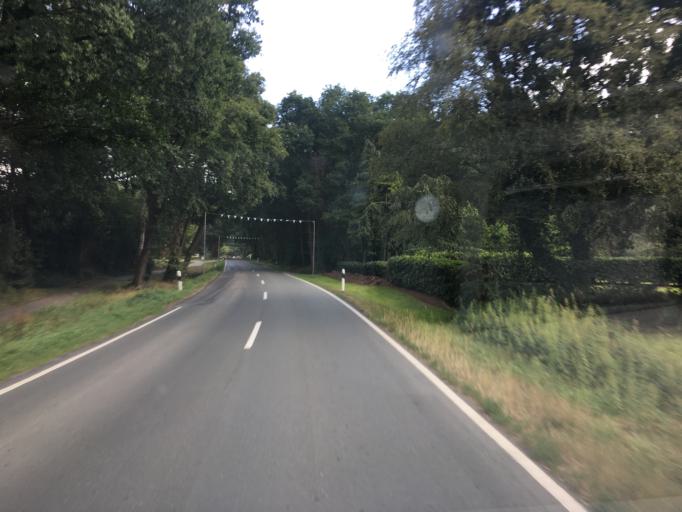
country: DE
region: Lower Saxony
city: Friesoythe
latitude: 53.0792
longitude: 7.8387
